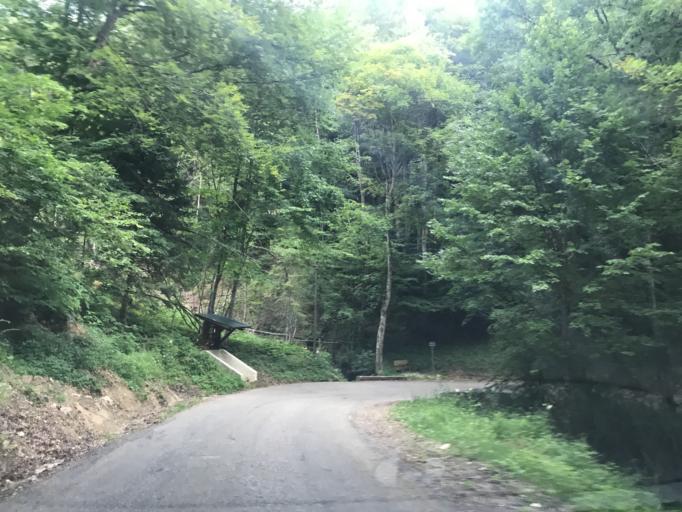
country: FR
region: Rhone-Alpes
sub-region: Departement de l'Isere
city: Saint-Vincent-de-Mercuze
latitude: 45.3859
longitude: 5.9321
